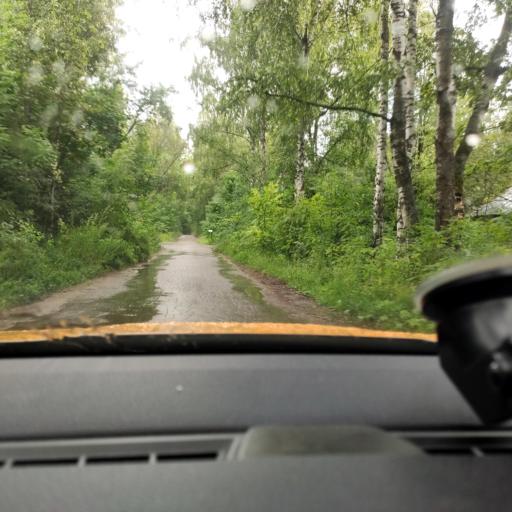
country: RU
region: Moscow
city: Babushkin
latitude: 55.8514
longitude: 37.7080
